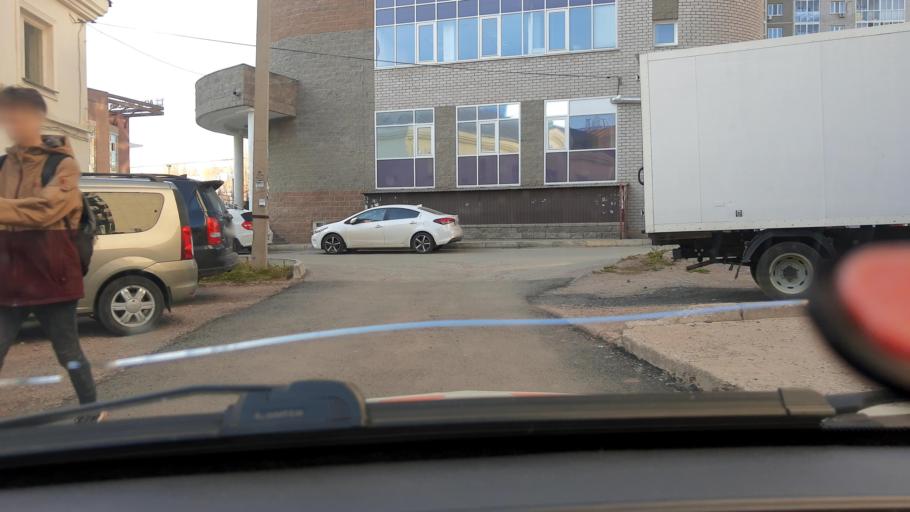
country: RU
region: Bashkortostan
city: Ufa
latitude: 54.7354
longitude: 55.9890
